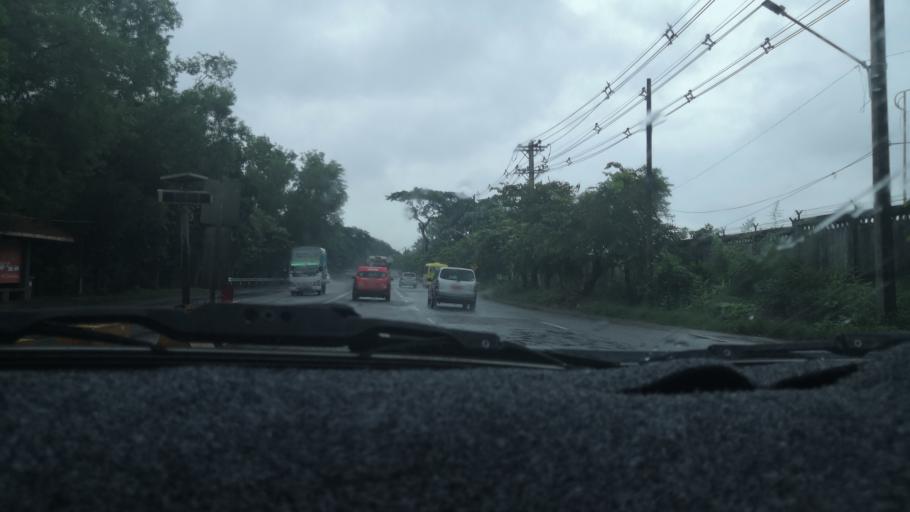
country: MM
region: Yangon
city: Yangon
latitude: 16.9114
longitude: 96.1325
